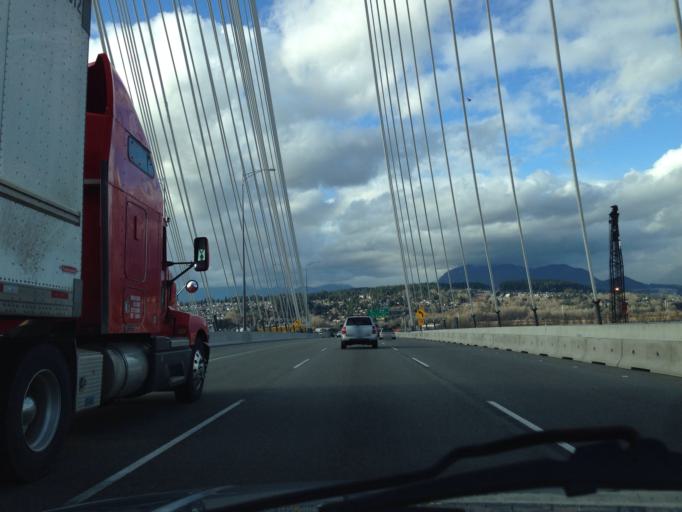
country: CA
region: British Columbia
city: Port Moody
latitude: 49.2198
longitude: -122.8130
